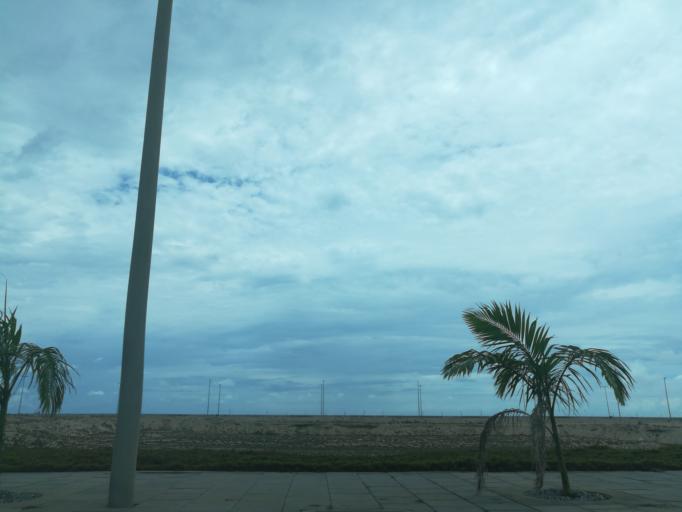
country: NG
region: Lagos
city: Ikoyi
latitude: 6.4079
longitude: 3.4198
